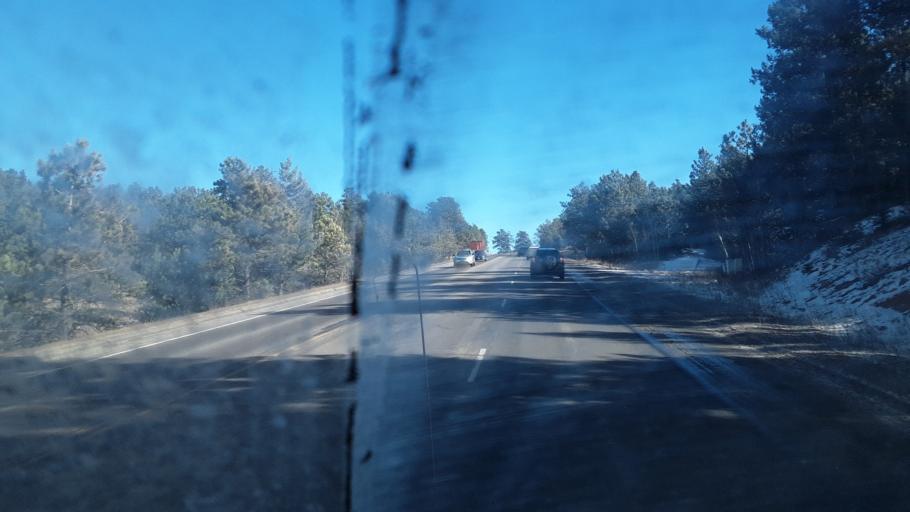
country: US
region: Colorado
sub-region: Jefferson County
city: Evergreen
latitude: 39.4620
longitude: -105.4048
